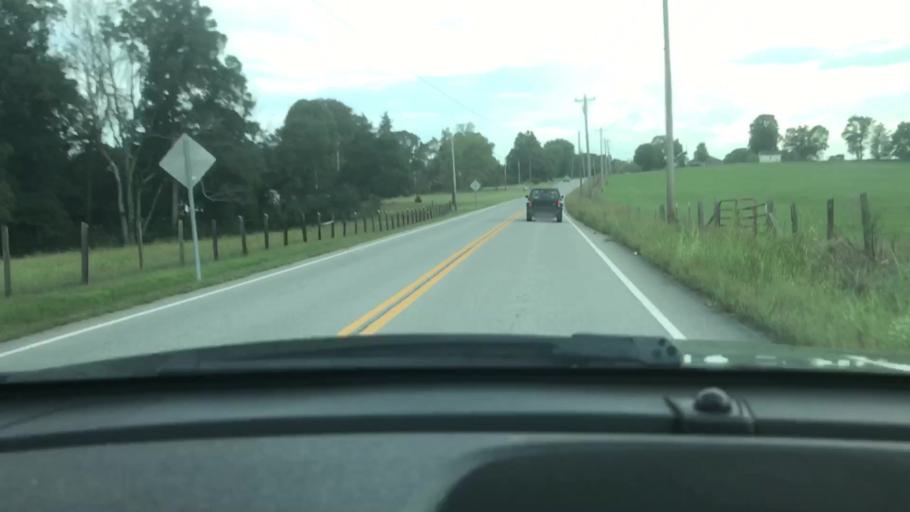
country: US
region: Tennessee
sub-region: Dickson County
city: Charlotte
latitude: 36.2376
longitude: -87.2465
